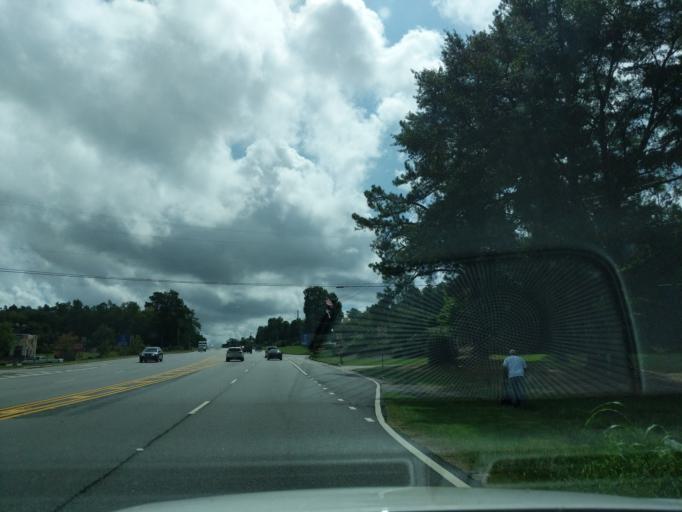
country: US
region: Georgia
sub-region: Columbia County
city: Evans
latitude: 33.5463
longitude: -82.1465
